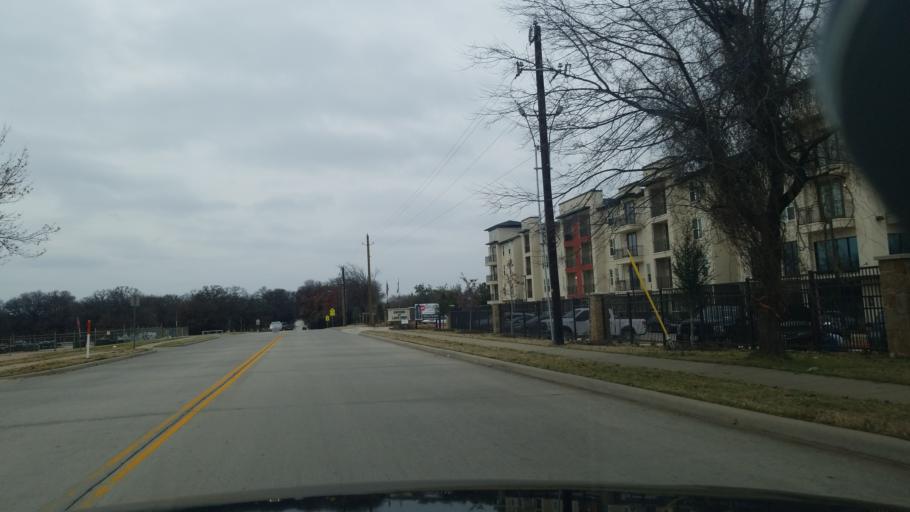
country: US
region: Texas
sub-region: Denton County
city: Hickory Creek
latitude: 33.1309
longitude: -97.0473
